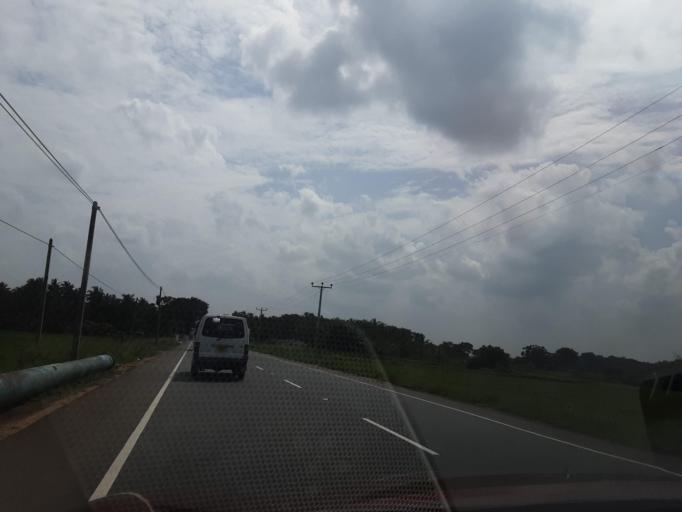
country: LK
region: North Central
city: Anuradhapura
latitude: 8.4750
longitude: 80.5128
